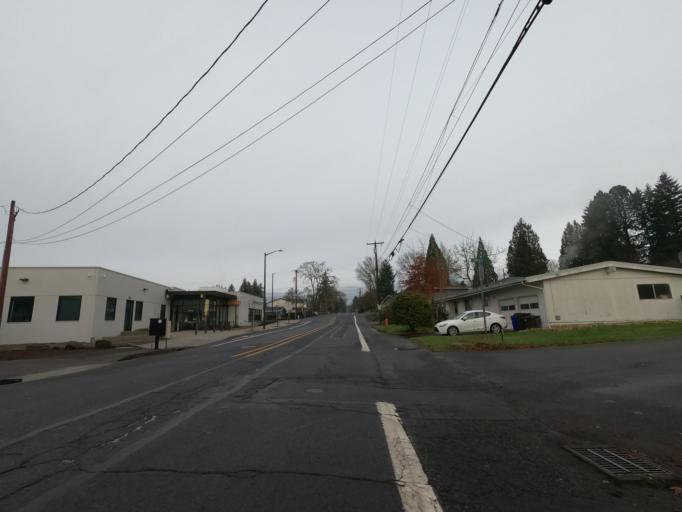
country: US
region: Oregon
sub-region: Clackamas County
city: Gladstone
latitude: 45.3881
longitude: -122.5998
